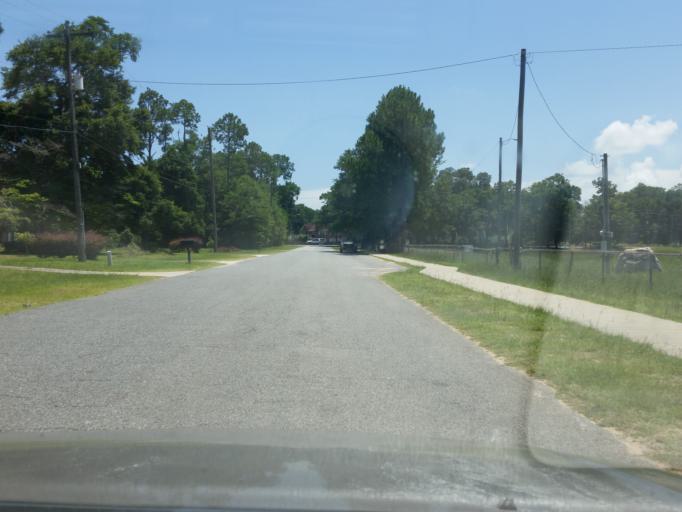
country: US
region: Florida
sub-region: Escambia County
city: Ferry Pass
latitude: 30.5118
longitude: -87.1970
